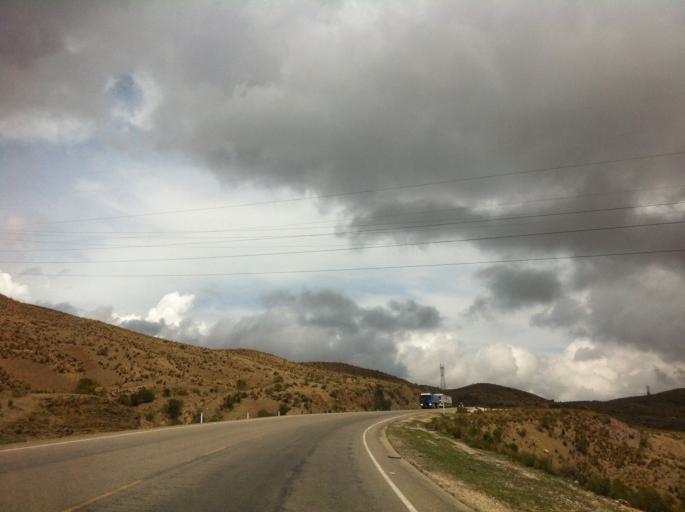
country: BO
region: Cochabamba
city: Irpa Irpa
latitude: -17.7093
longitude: -66.5347
